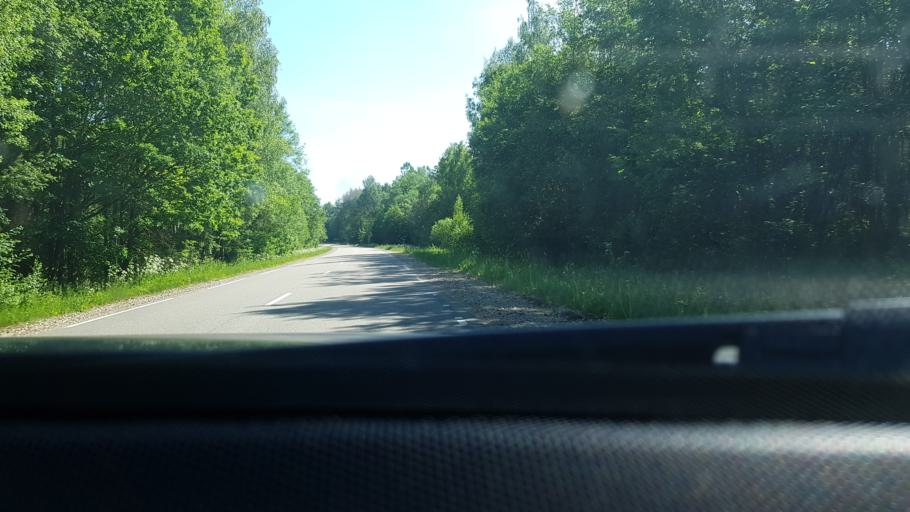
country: BY
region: Vitebsk
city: Braslaw
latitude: 55.8358
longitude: 26.9374
